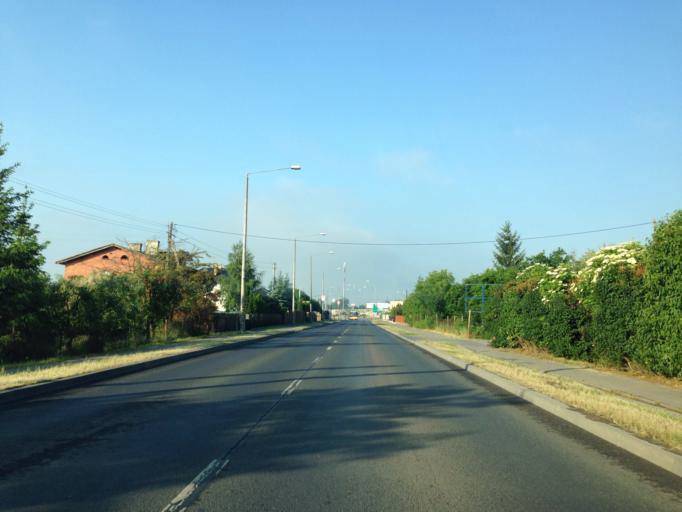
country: PL
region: Kujawsko-Pomorskie
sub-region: Grudziadz
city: Grudziadz
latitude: 53.5061
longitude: 18.8009
